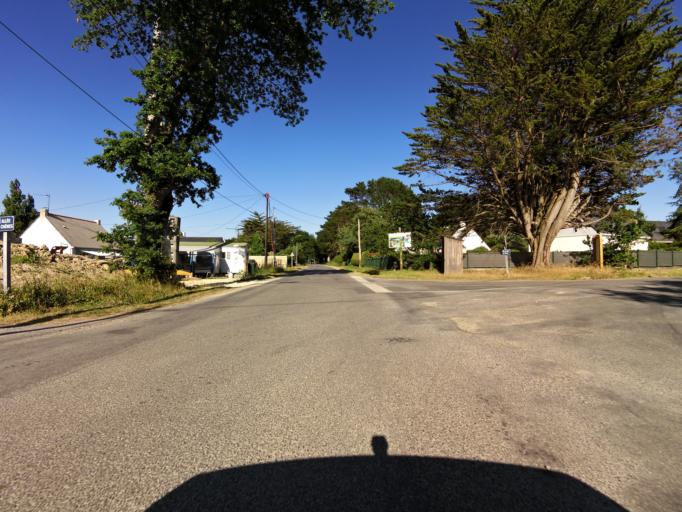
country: FR
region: Brittany
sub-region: Departement du Morbihan
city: Penestin
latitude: 47.4728
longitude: -2.4682
